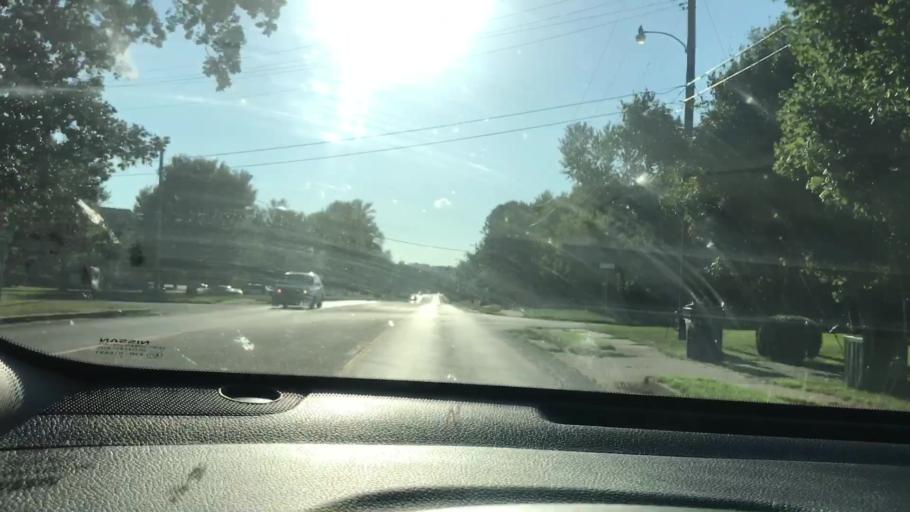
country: US
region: Kentucky
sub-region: Calloway County
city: Murray
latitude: 36.5956
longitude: -88.3103
